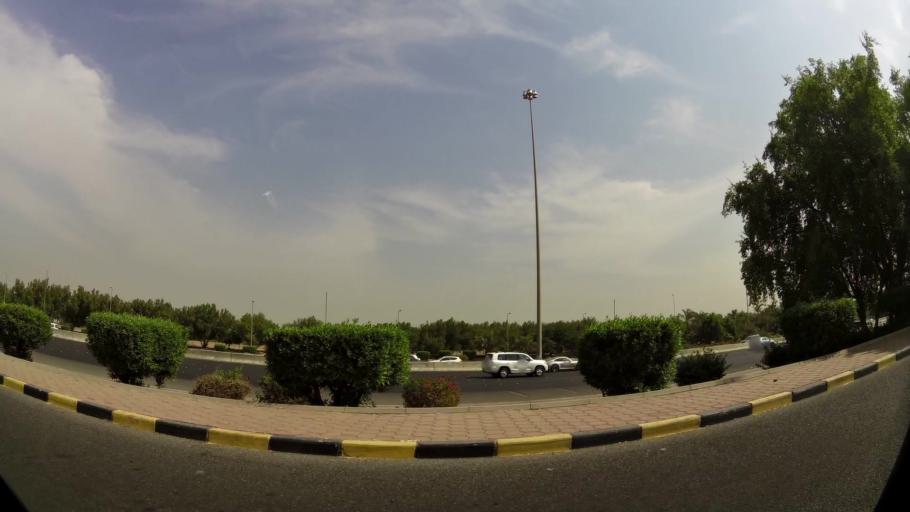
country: KW
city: Bayan
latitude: 29.2813
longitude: 48.0338
